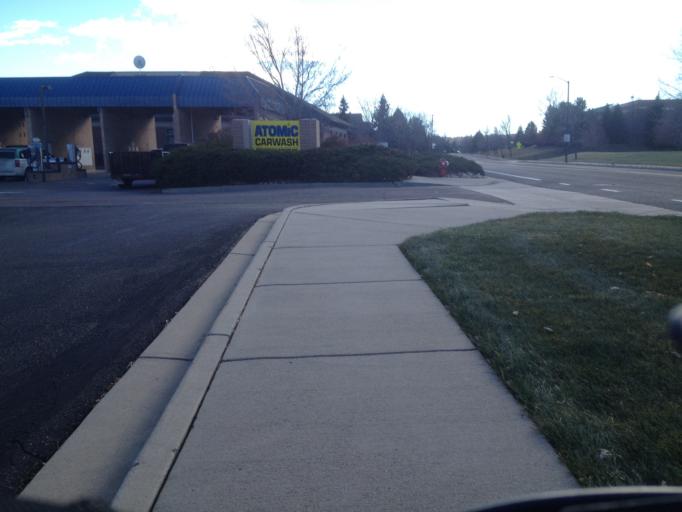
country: US
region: Colorado
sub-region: Boulder County
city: Superior
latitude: 39.9644
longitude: -105.1589
